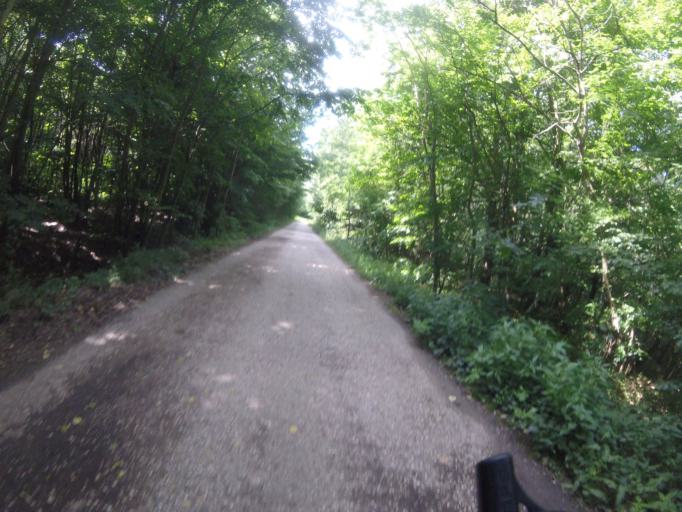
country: HU
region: Fejer
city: Szarliget
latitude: 47.4875
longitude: 18.4805
